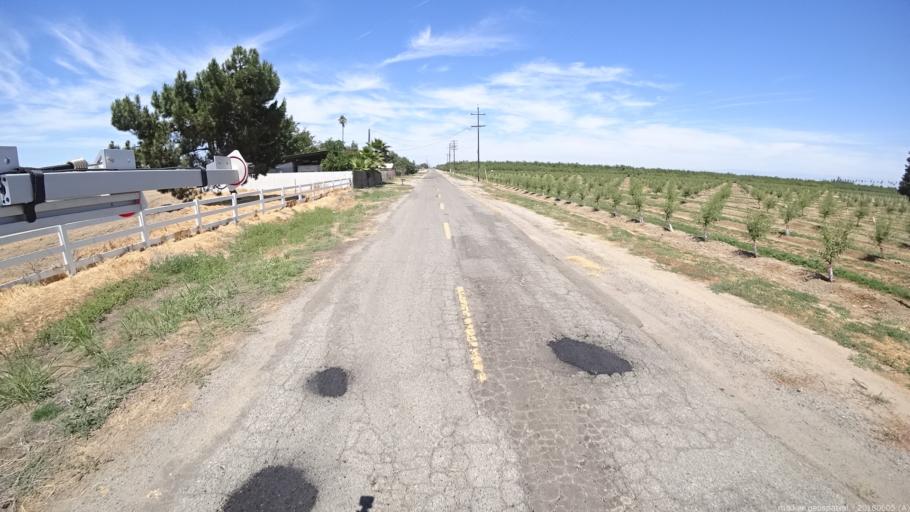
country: US
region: California
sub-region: Madera County
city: Chowchilla
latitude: 37.0966
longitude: -120.2927
